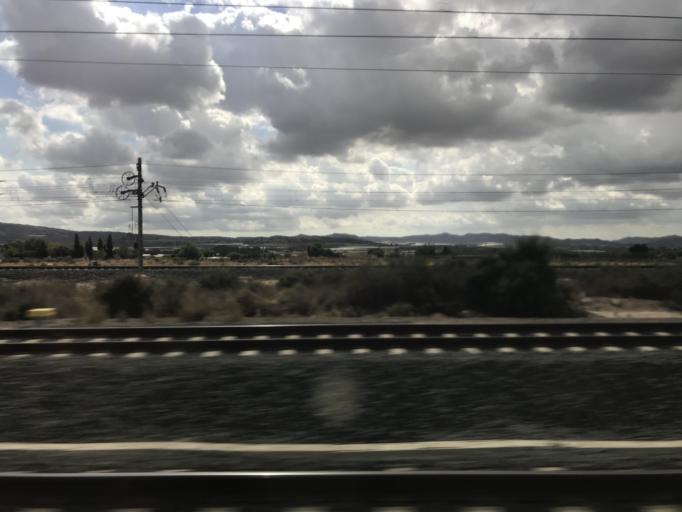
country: ES
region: Valencia
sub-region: Provincia de Alicante
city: Monforte del Cid
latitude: 38.4067
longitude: -0.6996
